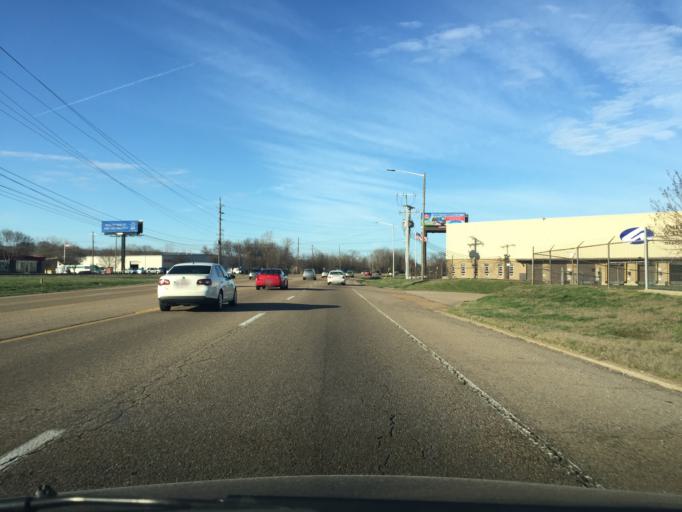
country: US
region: Tennessee
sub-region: Hamilton County
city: East Chattanooga
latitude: 35.0612
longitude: -85.2741
